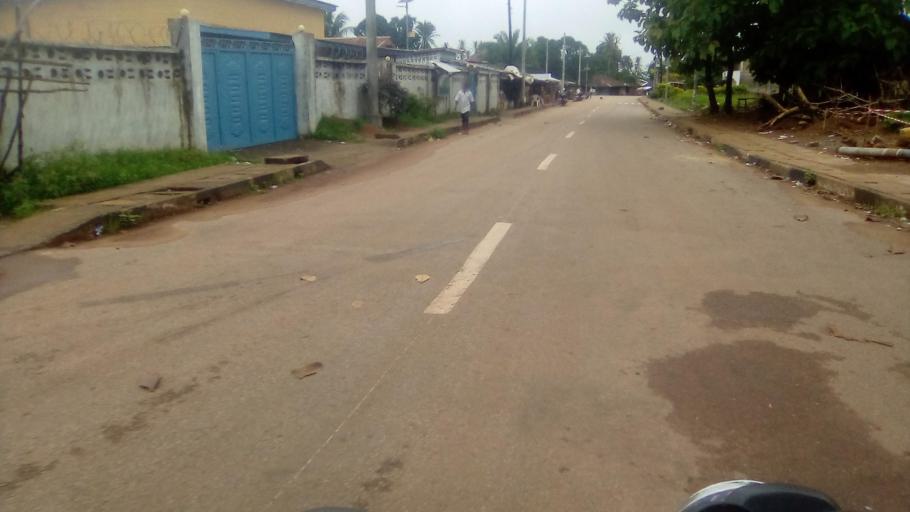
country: SL
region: Southern Province
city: Moyamba
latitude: 8.1603
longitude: -12.4332
